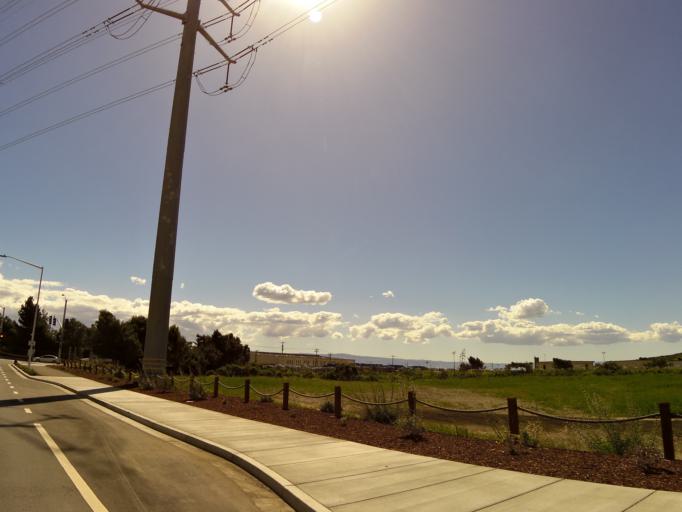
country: US
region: California
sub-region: Santa Clara County
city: Milpitas
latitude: 37.4562
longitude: -121.9268
